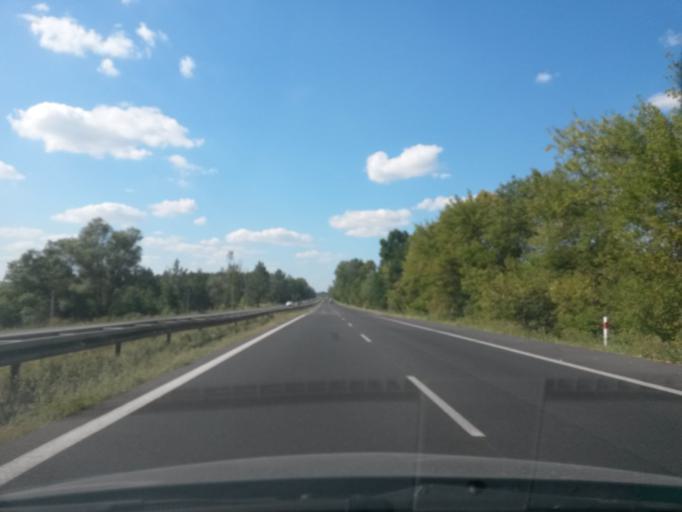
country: PL
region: Masovian Voivodeship
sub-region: Powiat nowodworski
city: Nowy Dwor Mazowiecki
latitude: 52.3970
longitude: 20.7161
